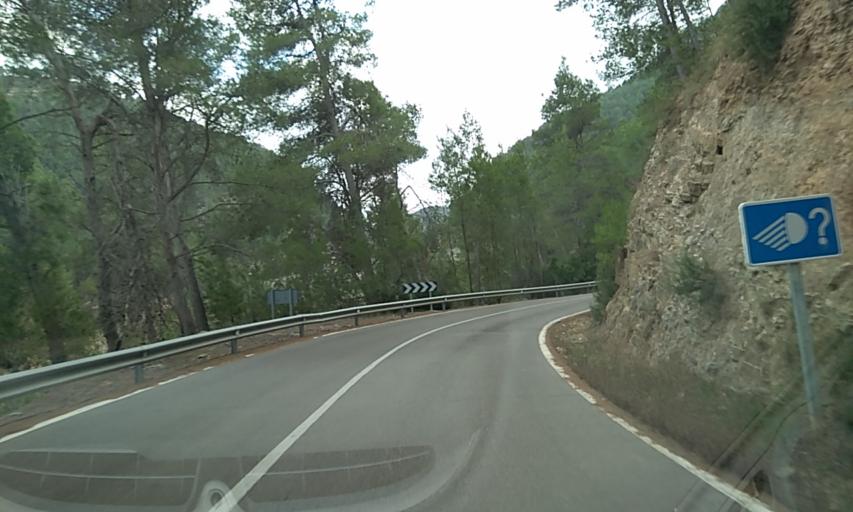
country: ES
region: Valencia
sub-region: Provincia de Castello
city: Montanejos
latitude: 40.0851
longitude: -0.5414
